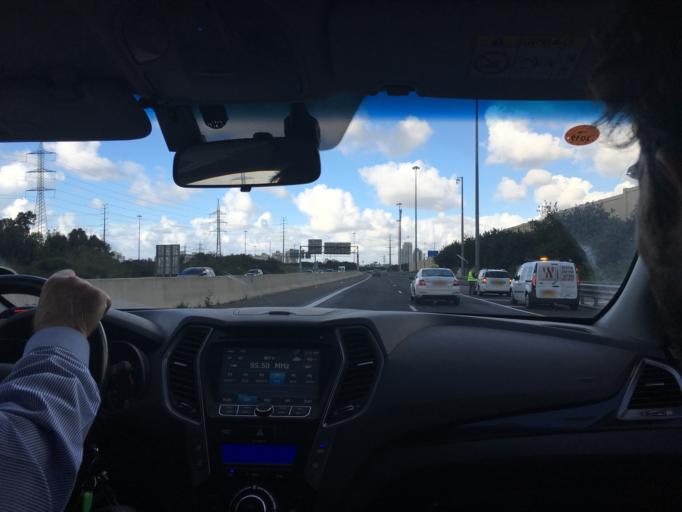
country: IL
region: Central District
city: Rishon LeZiyyon
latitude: 31.9574
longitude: 34.7855
